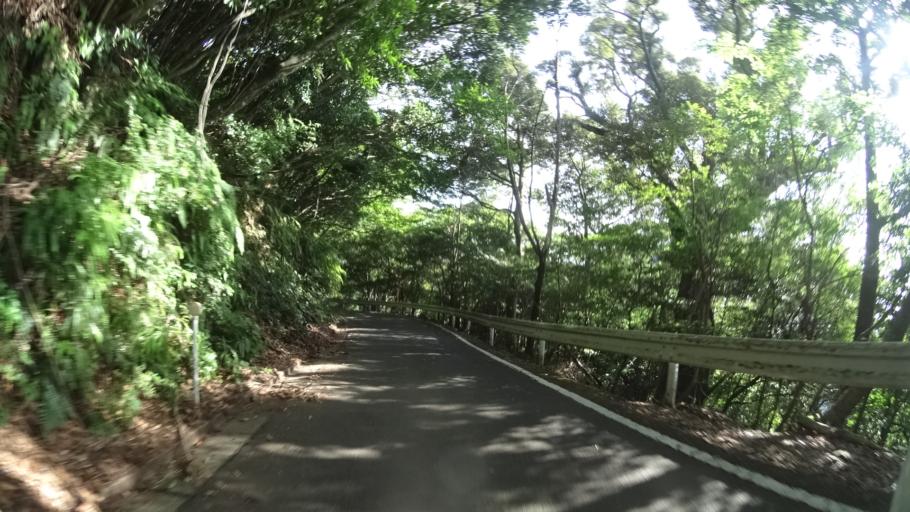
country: JP
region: Kagoshima
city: Nishinoomote
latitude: 30.3381
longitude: 130.3962
